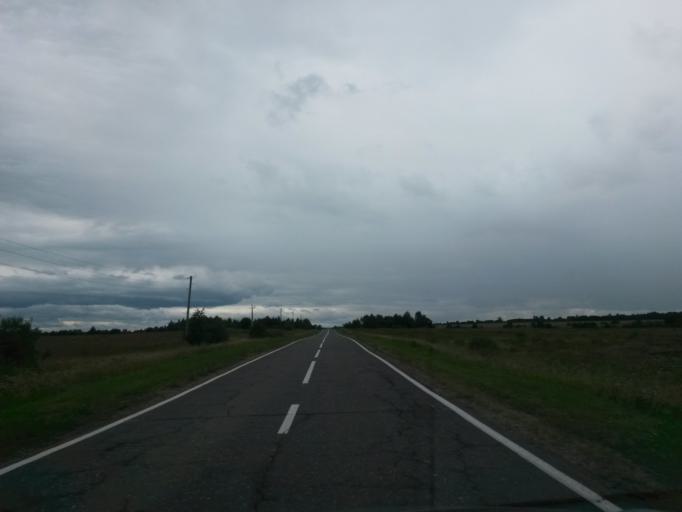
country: RU
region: Jaroslavl
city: Tutayev
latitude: 57.9484
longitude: 39.4691
